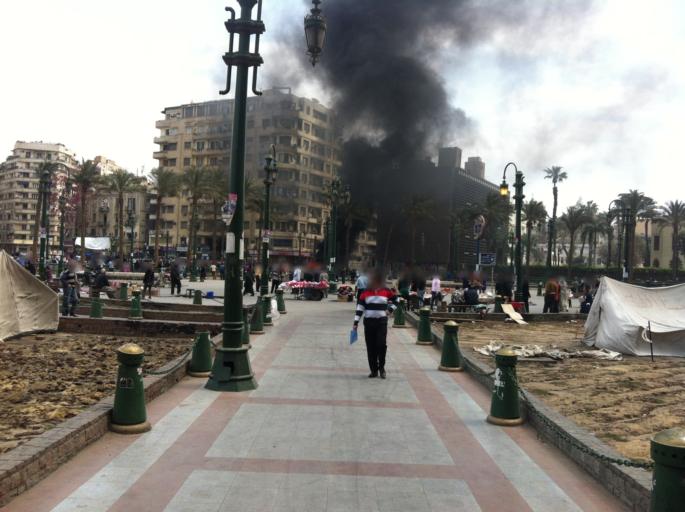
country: EG
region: Muhafazat al Qahirah
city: Cairo
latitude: 30.0432
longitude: 31.2348
